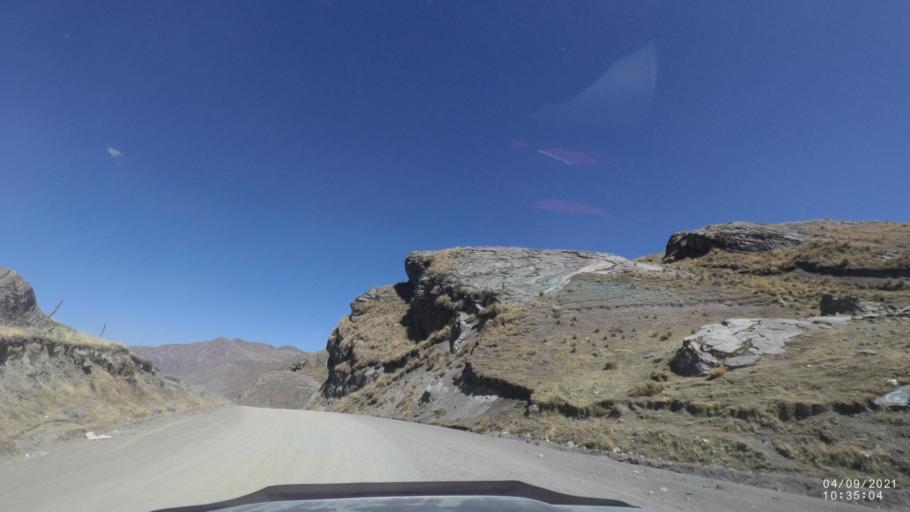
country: BO
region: Cochabamba
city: Sipe Sipe
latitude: -17.2898
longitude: -66.4456
